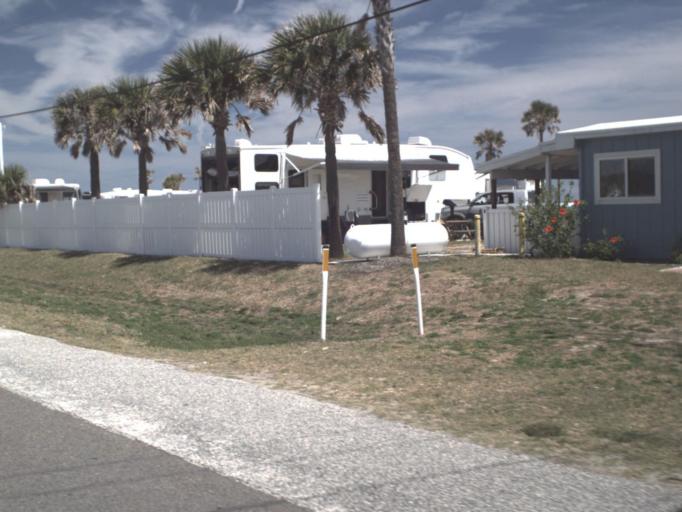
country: US
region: Florida
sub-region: Flagler County
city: Flagler Beach
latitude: 29.5228
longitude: -81.1484
